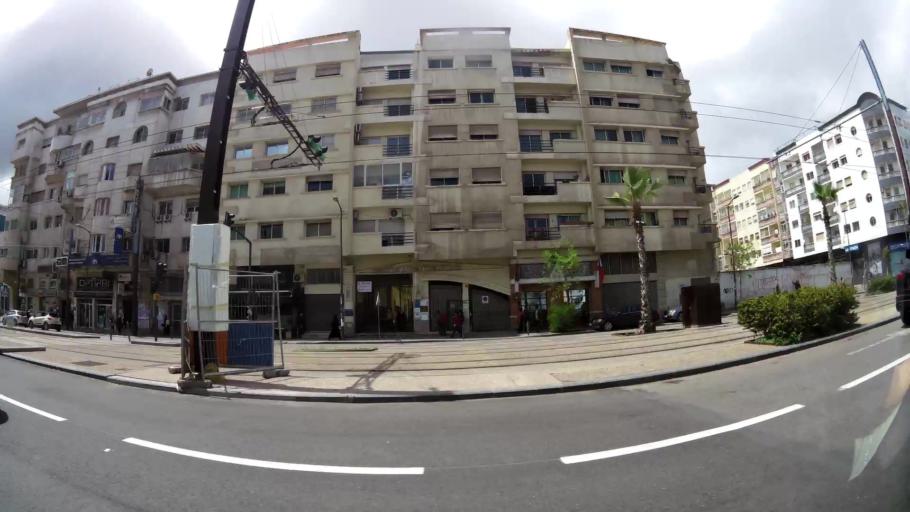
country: MA
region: Grand Casablanca
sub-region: Casablanca
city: Casablanca
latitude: 33.5702
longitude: -7.6257
